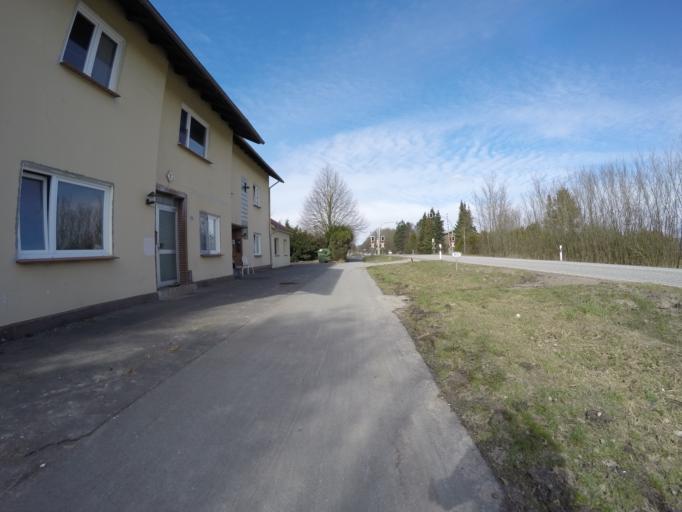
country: DE
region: Schleswig-Holstein
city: Bilsen
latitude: 53.7912
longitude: 9.8759
